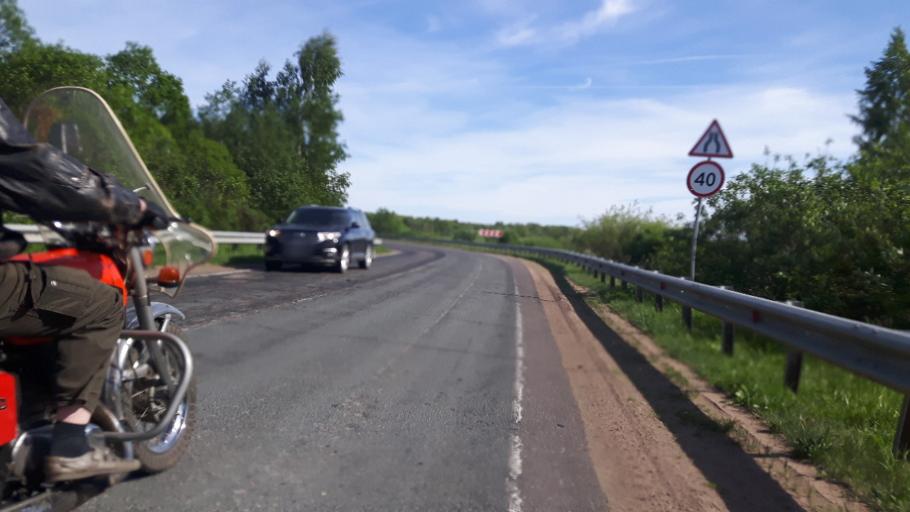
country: RU
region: Leningrad
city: Ivangorod
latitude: 59.4159
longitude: 28.3265
